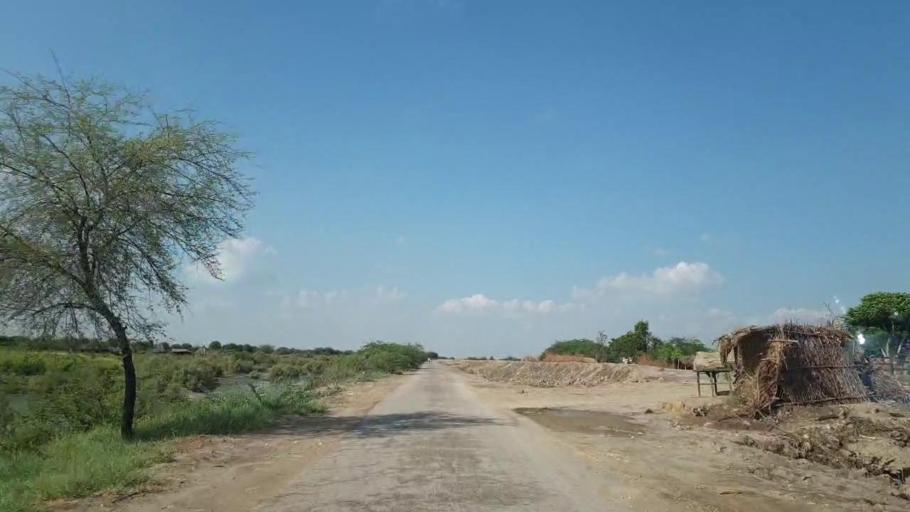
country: PK
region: Sindh
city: Pithoro
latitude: 25.6283
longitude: 69.4332
